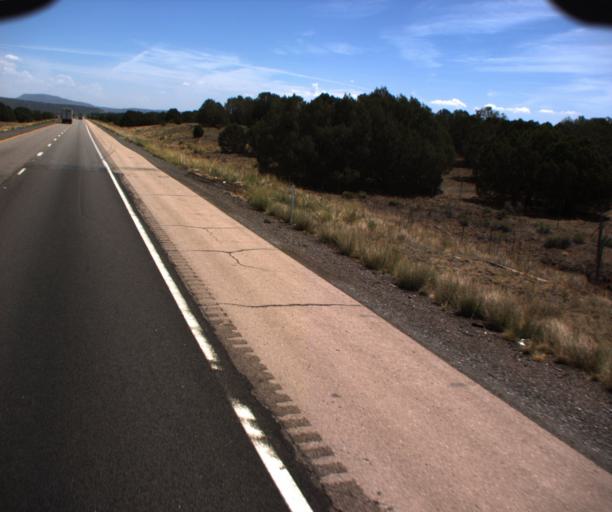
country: US
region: Arizona
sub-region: Mohave County
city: Peach Springs
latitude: 35.2120
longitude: -113.2612
